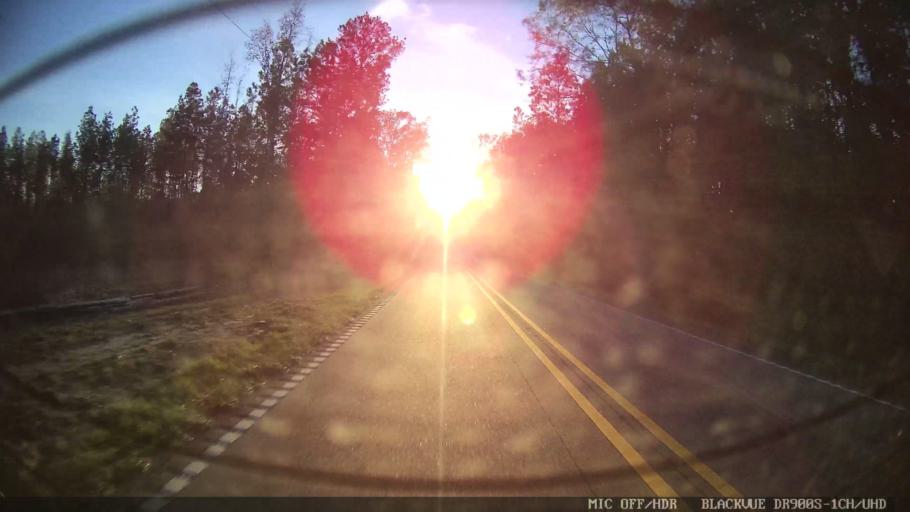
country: US
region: Mississippi
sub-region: Lamar County
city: Lumberton
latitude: 30.9989
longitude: -89.3593
